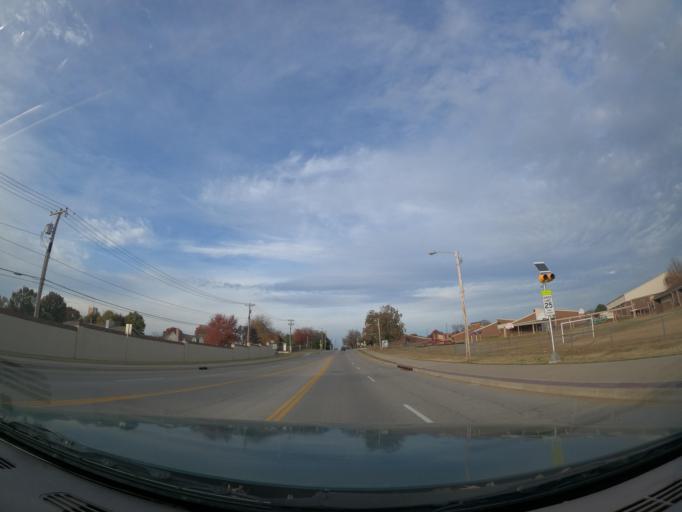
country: US
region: Oklahoma
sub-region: Tulsa County
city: Jenks
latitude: 36.0329
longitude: -95.9399
